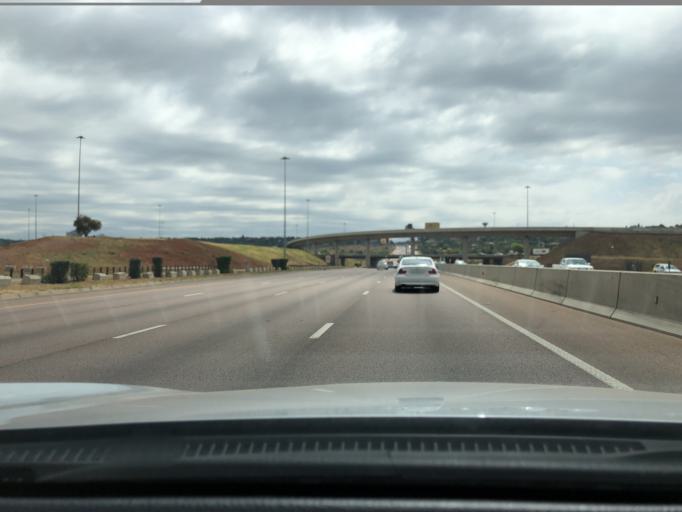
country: ZA
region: Gauteng
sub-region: City of Tshwane Metropolitan Municipality
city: Centurion
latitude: -25.8317
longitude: 28.2410
